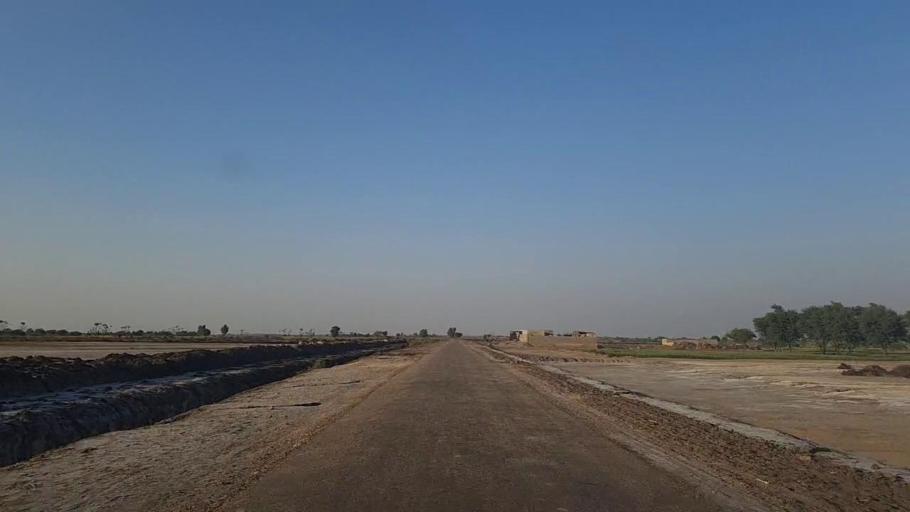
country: PK
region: Sindh
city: Jam Sahib
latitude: 26.3321
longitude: 68.6677
